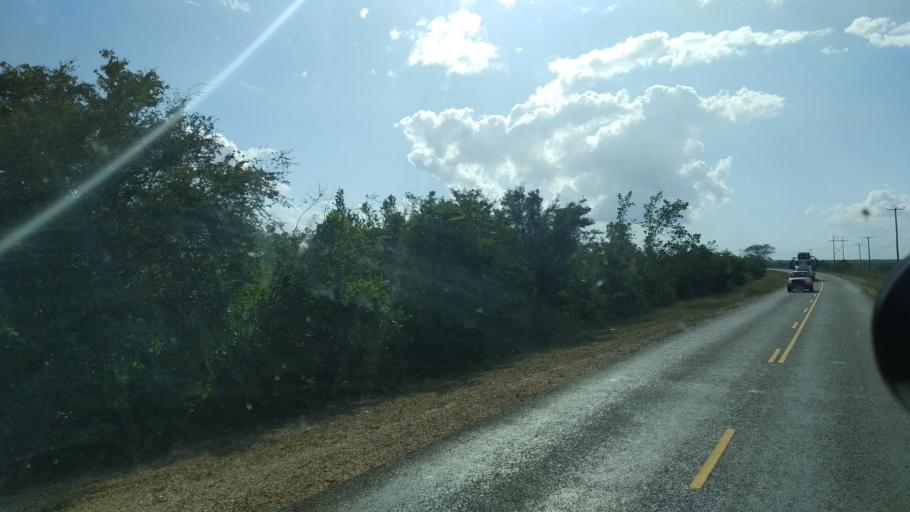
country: BZ
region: Belize
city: Belize City
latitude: 17.4070
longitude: -88.4645
